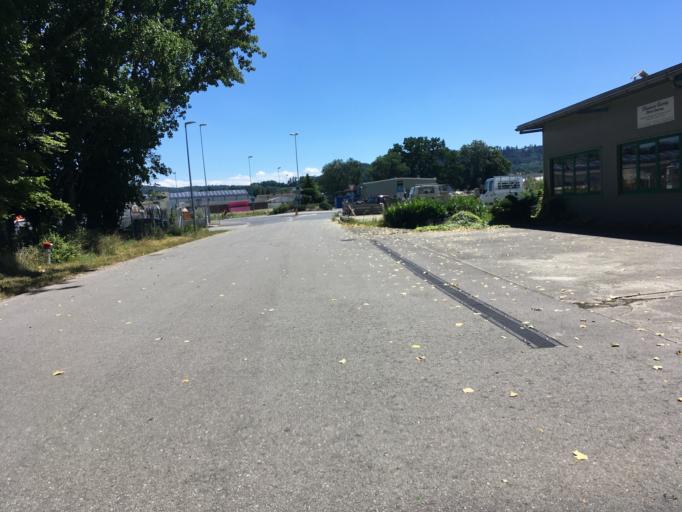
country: CH
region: Vaud
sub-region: Broye-Vully District
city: Avenches
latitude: 46.8898
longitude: 7.0427
